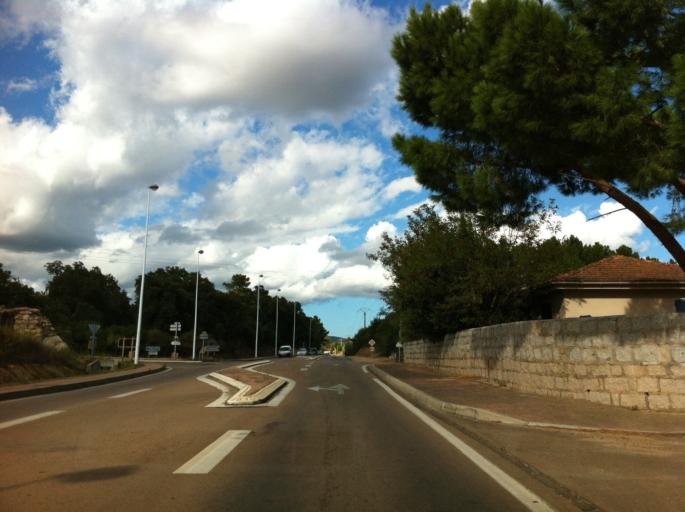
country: FR
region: Corsica
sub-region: Departement de la Corse-du-Sud
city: Porto-Vecchio
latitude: 41.6288
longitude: 9.2910
